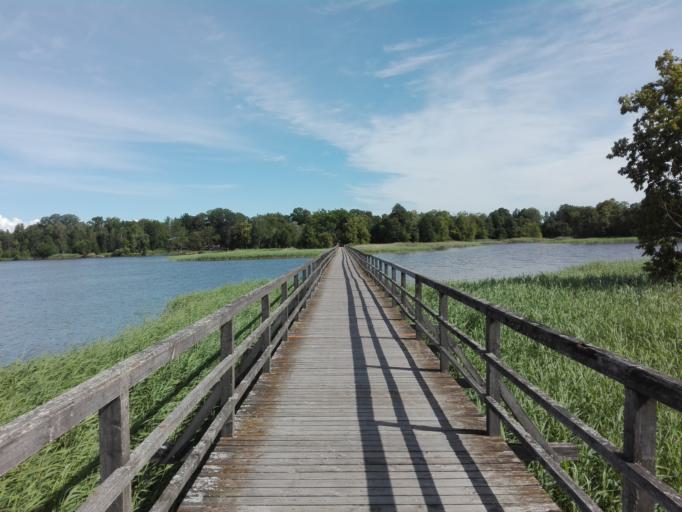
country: LT
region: Panevezys
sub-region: Birzai
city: Birzai
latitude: 56.2146
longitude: 24.7696
